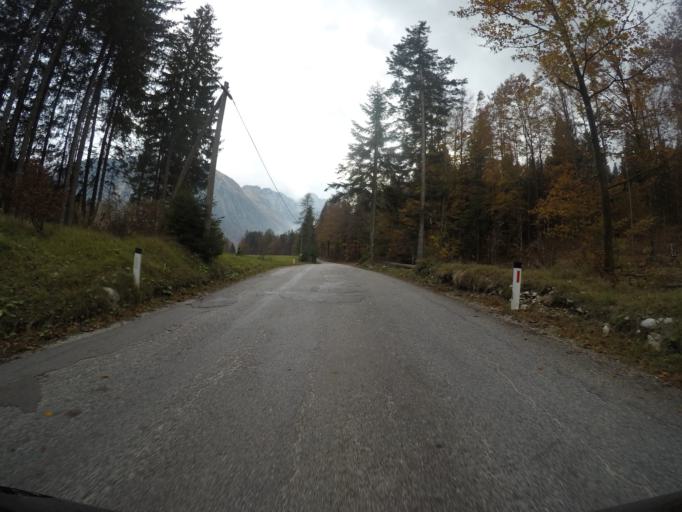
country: SI
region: Kranjska Gora
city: Mojstrana
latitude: 46.4375
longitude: 13.9310
